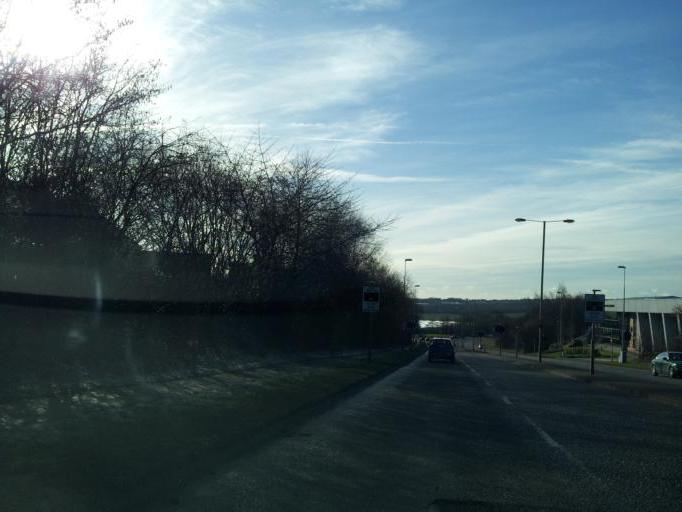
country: GB
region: England
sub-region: Staffordshire
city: Kidsgrove
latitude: 53.0678
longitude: -2.2185
